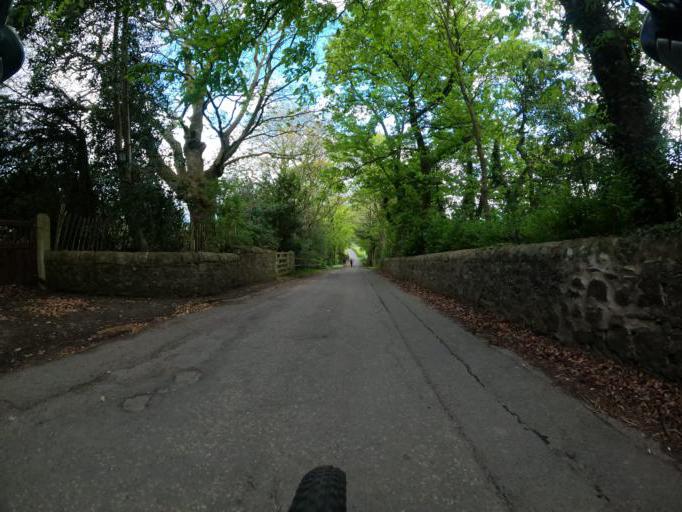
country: GB
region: Scotland
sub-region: Edinburgh
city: Ratho
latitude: 55.9543
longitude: -3.3434
